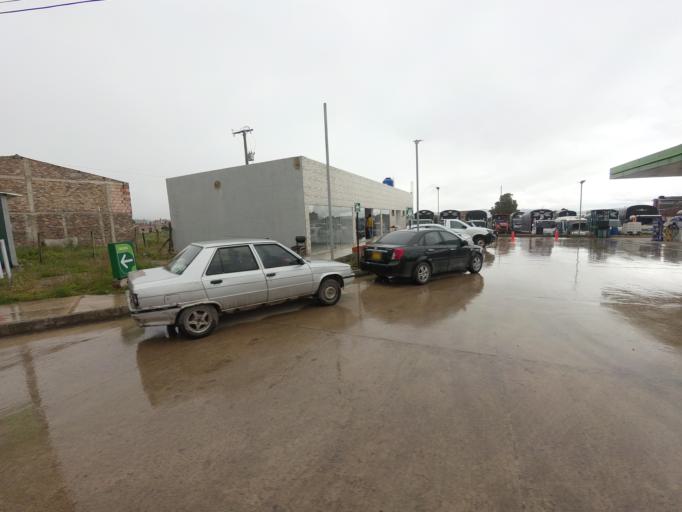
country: CO
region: Boyaca
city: Aquitania
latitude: 5.5238
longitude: -72.8832
